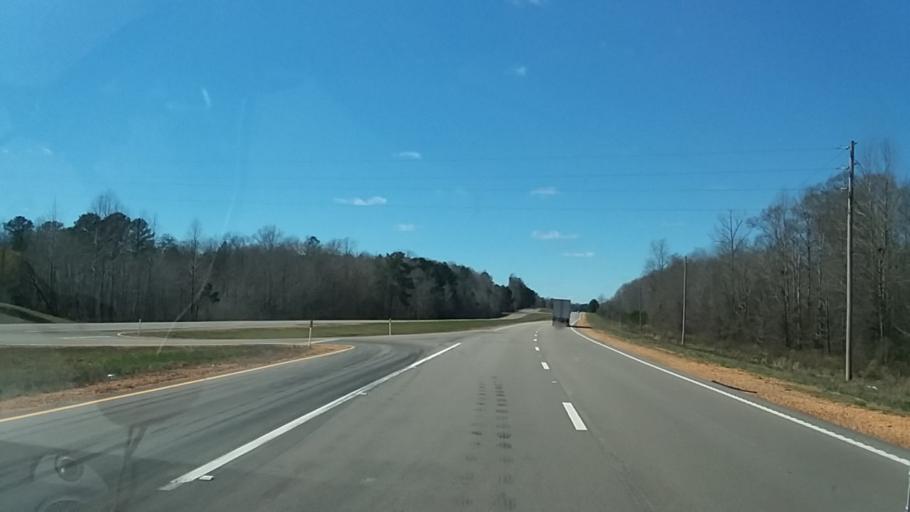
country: US
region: Mississippi
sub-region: Alcorn County
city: Farmington
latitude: 34.8570
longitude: -88.3886
